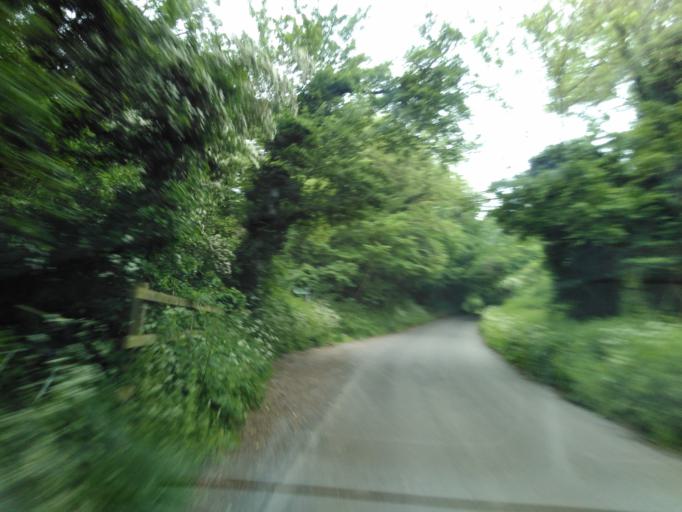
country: GB
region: England
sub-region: Kent
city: Chartham
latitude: 51.2629
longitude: 1.0475
